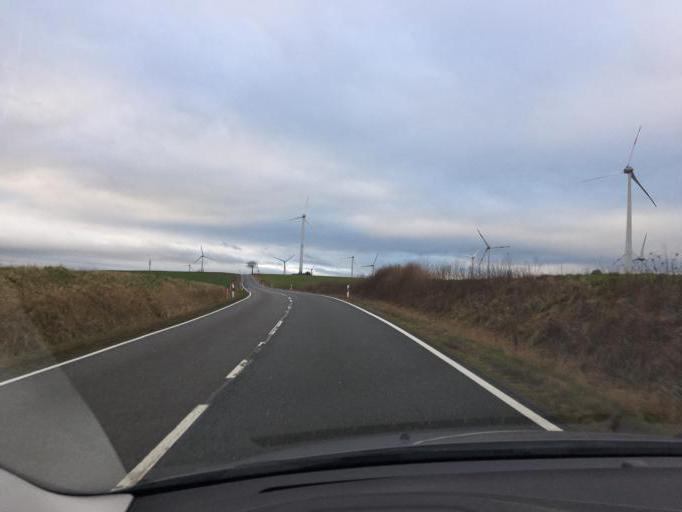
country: DE
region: Saxony
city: Penig
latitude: 50.9381
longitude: 12.6723
